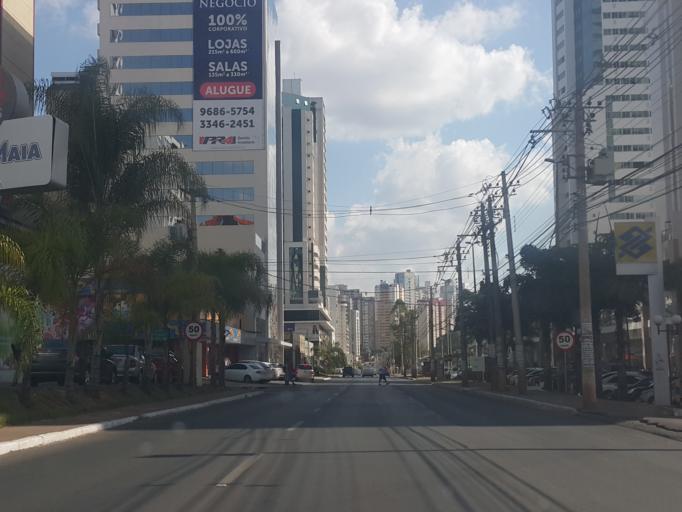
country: BR
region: Federal District
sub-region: Brasilia
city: Brasilia
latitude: -15.8354
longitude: -48.0179
